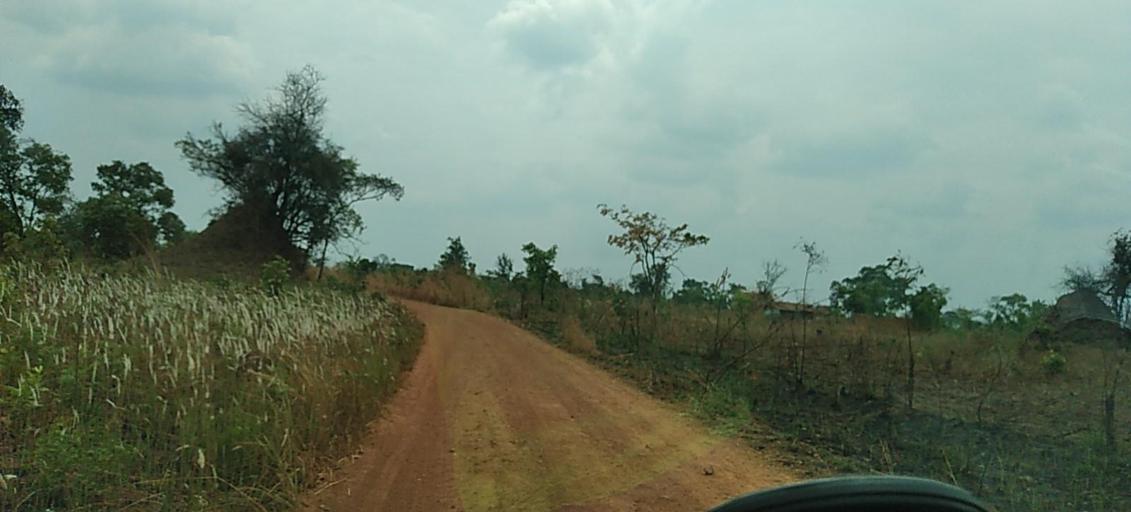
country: ZM
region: North-Western
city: Kansanshi
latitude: -12.0848
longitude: 26.3631
